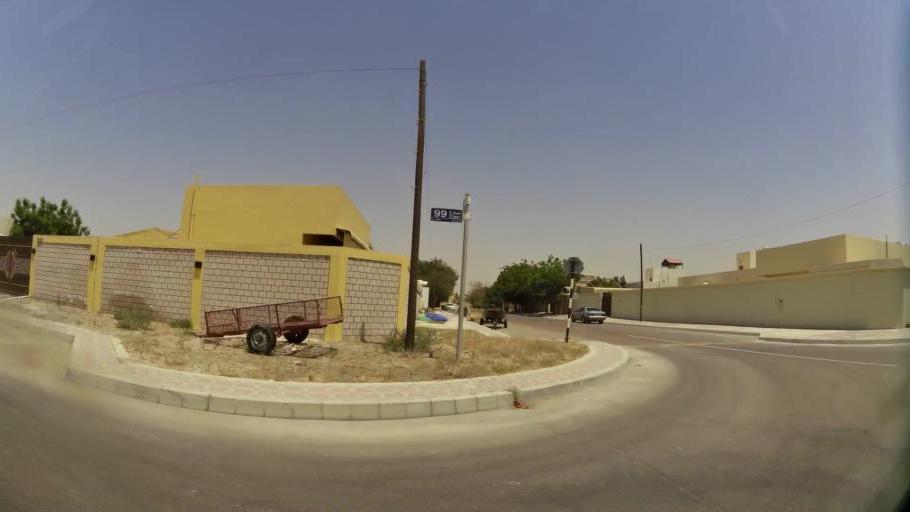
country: AE
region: Ajman
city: Ajman
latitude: 25.4192
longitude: 55.5043
